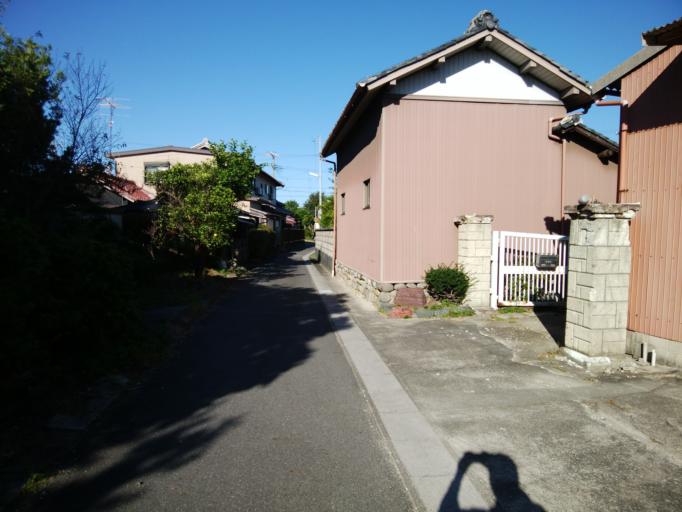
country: JP
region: Aichi
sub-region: Aisai-shi
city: Aisai
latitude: 35.1576
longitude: 136.7520
